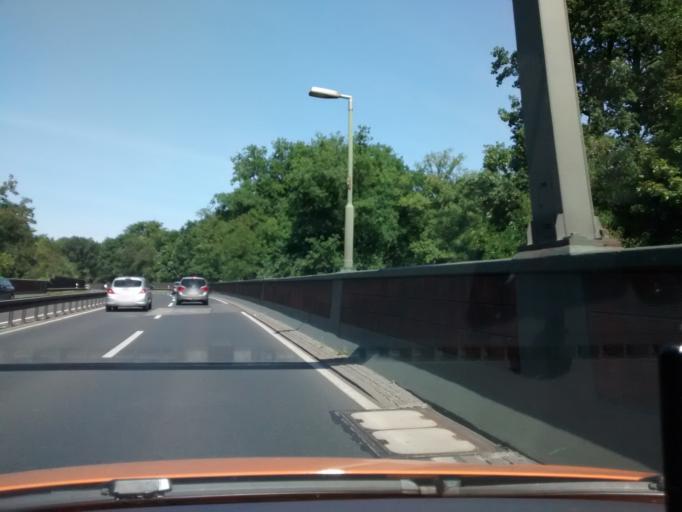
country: DE
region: Berlin
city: Tegel
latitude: 52.5998
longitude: 13.2816
